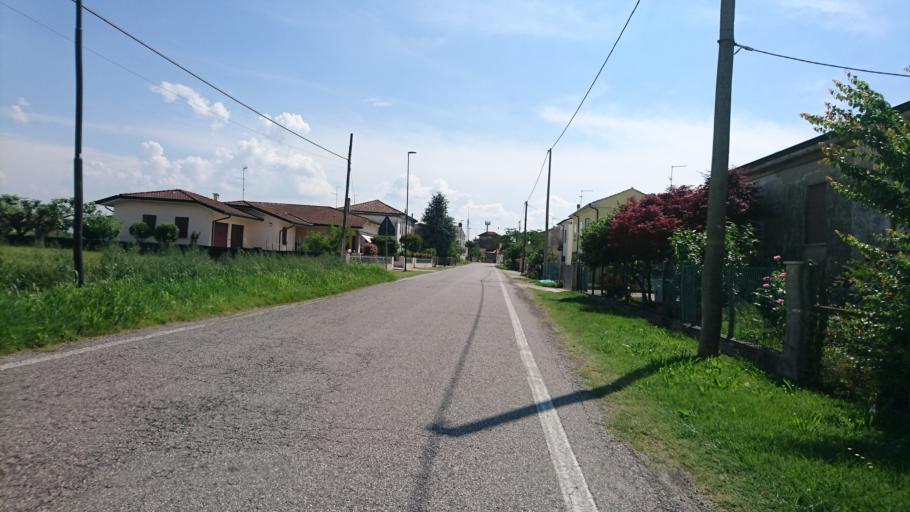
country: IT
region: Veneto
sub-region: Provincia di Rovigo
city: Castelmassa
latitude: 45.0609
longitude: 11.3328
